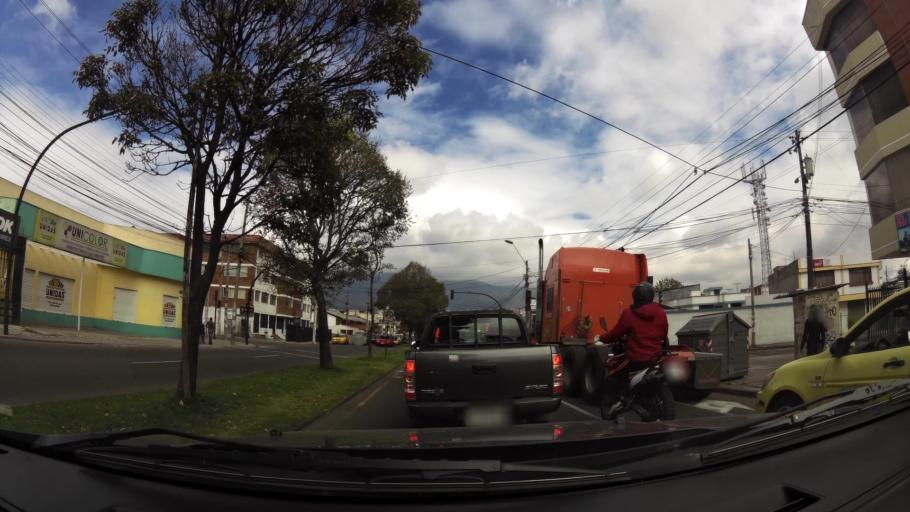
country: EC
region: Pichincha
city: Quito
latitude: -0.1541
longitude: -78.4710
